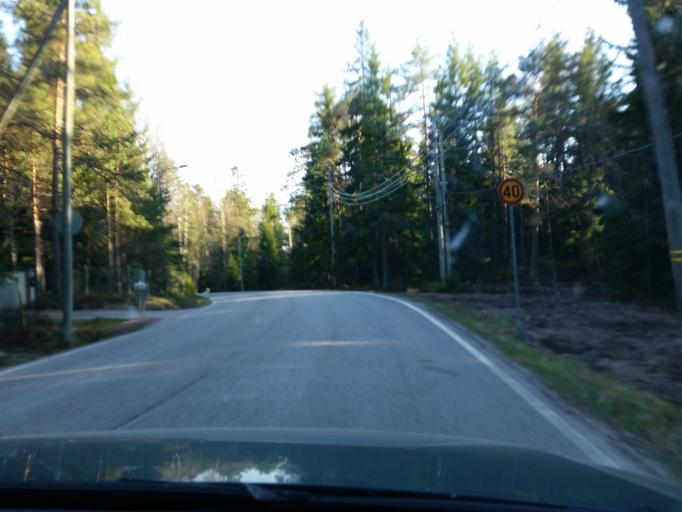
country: FI
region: Uusimaa
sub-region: Helsinki
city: Espoo
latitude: 60.1064
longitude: 24.5680
